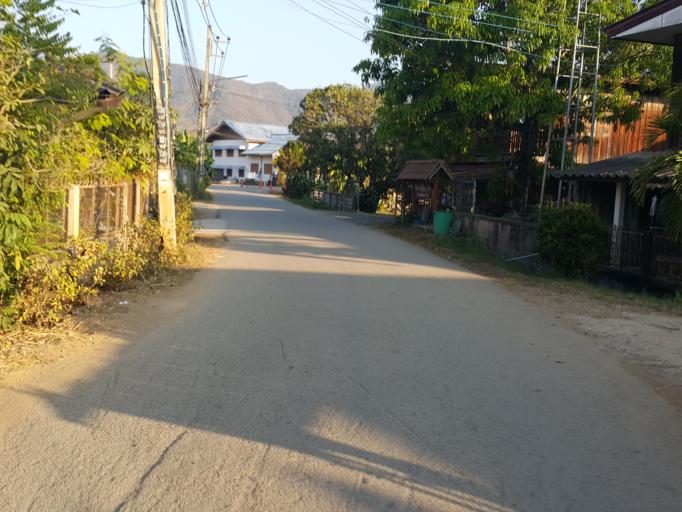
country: TH
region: Chiang Mai
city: Mae On
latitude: 18.7856
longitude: 99.2567
